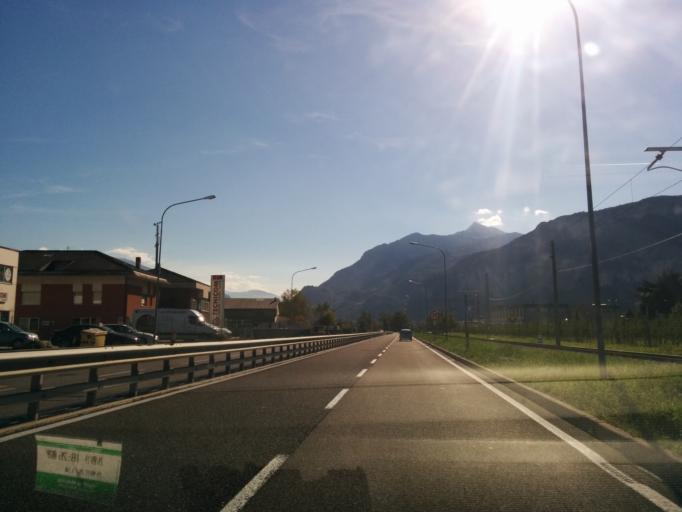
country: IT
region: Trentino-Alto Adige
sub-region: Provincia di Trento
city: Meano
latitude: 46.1235
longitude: 11.1069
